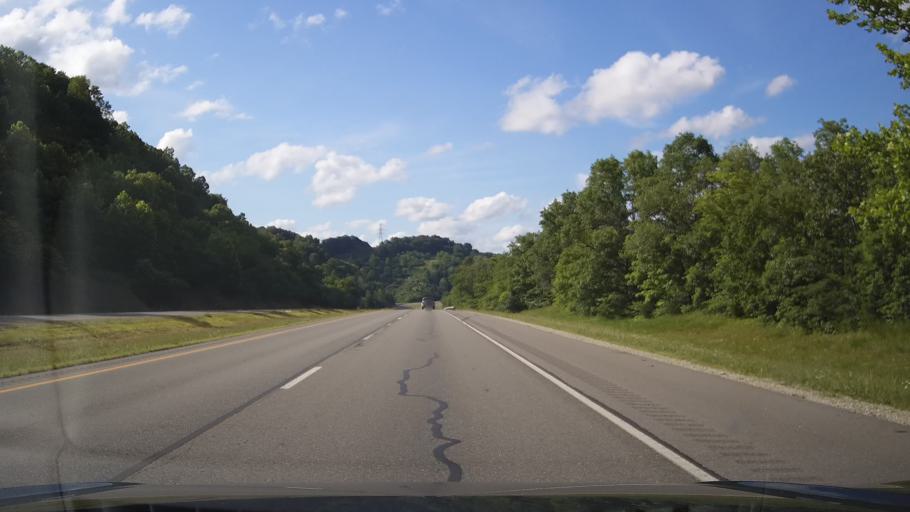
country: US
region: Kentucky
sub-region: Lawrence County
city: Louisa
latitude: 38.2275
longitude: -82.6118
